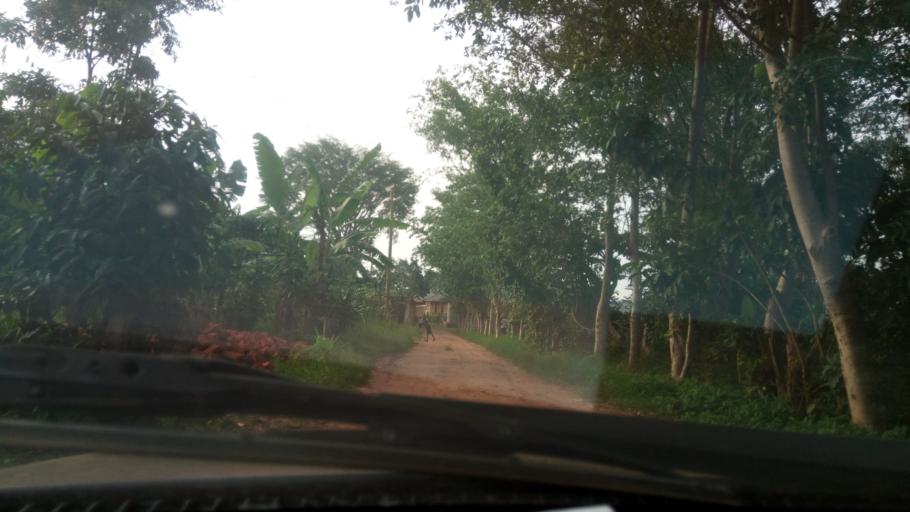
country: UG
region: Central Region
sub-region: Mityana District
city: Mityana
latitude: 0.5600
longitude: 32.1969
